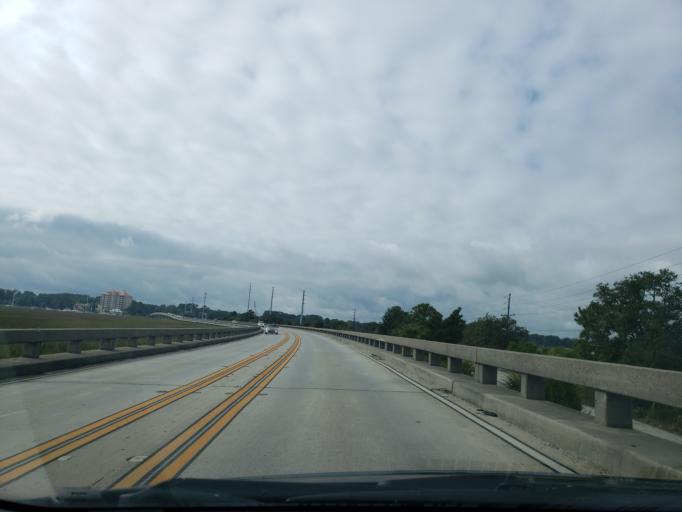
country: US
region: Georgia
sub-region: Chatham County
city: Wilmington Island
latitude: 32.0399
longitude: -80.9529
